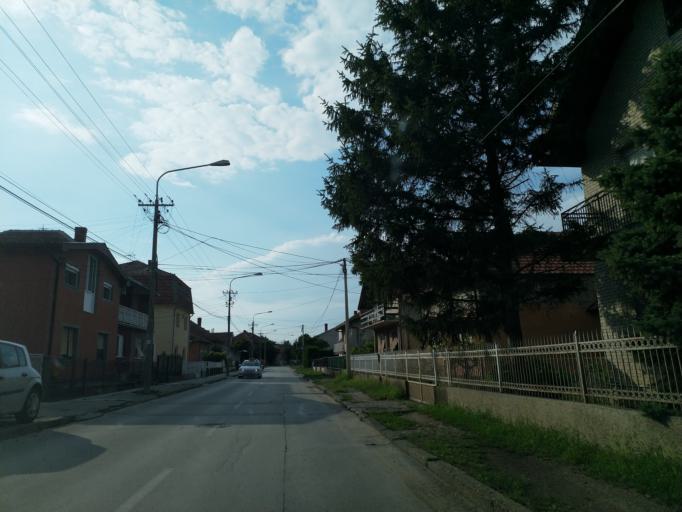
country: RS
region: Central Serbia
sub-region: Pomoravski Okrug
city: Jagodina
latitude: 43.9751
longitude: 21.2516
